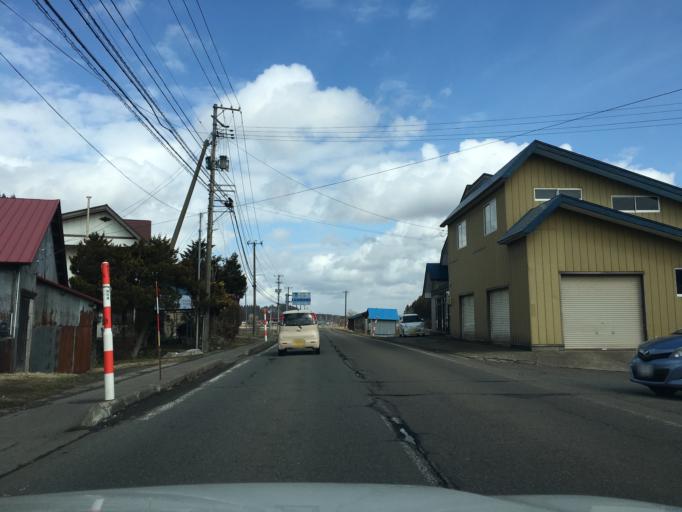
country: JP
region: Akita
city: Takanosu
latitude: 40.0346
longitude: 140.2756
